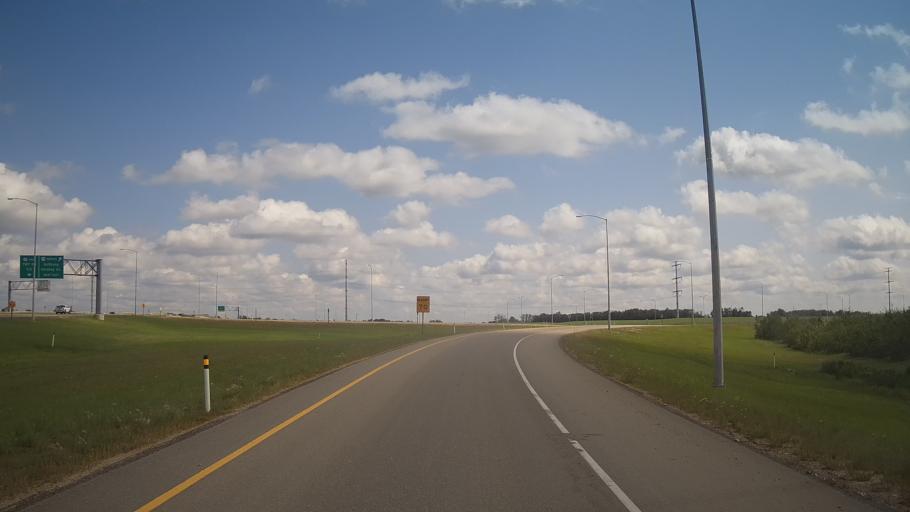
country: CA
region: Alberta
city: Sherwood Park
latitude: 53.4825
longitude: -113.3483
